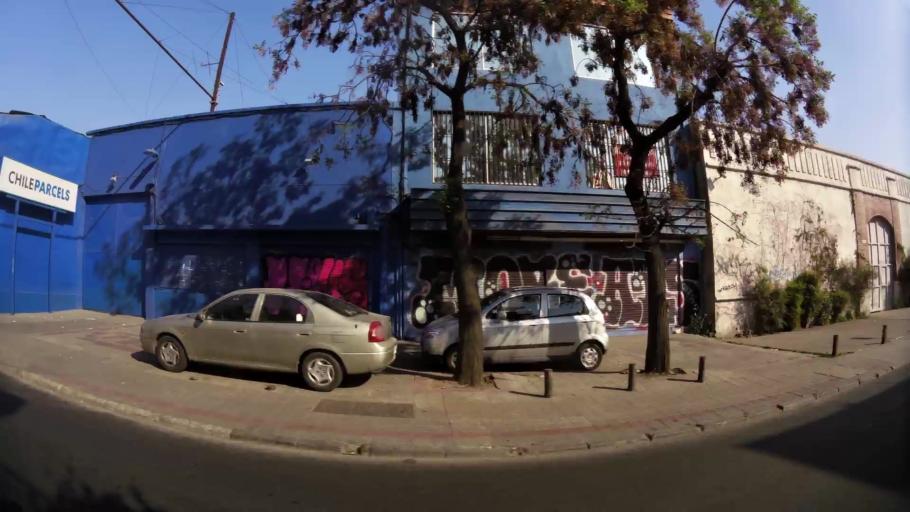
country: CL
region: Santiago Metropolitan
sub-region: Provincia de Santiago
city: Santiago
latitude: -33.4396
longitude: -70.6626
